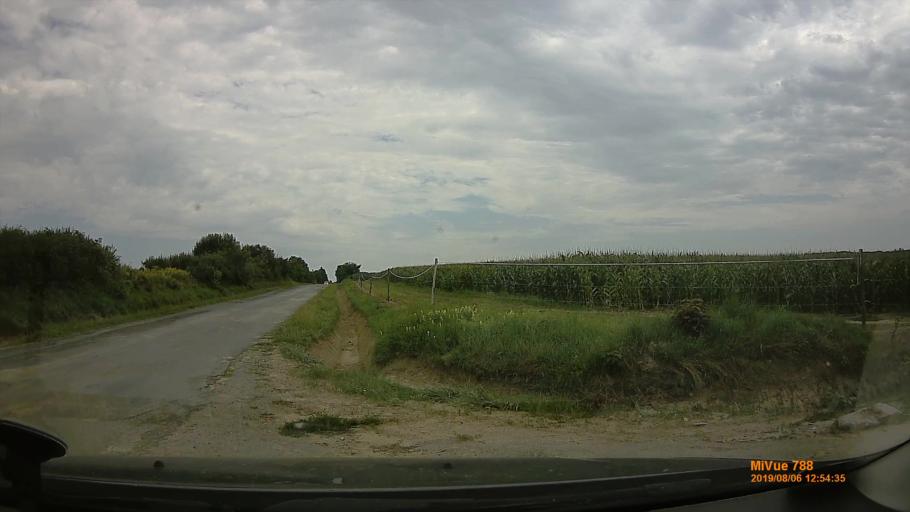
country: HU
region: Zala
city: Pacsa
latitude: 46.6371
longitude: 17.0137
